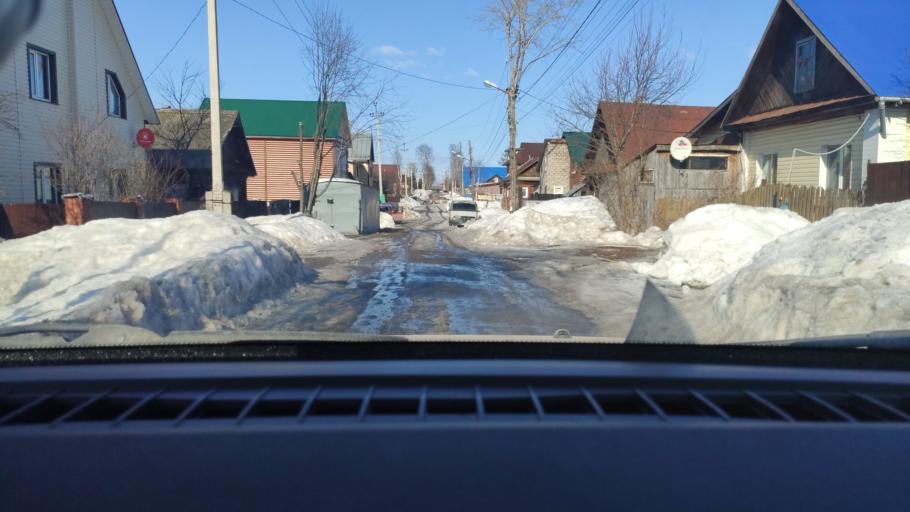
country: RU
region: Perm
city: Perm
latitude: 58.0403
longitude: 56.3571
